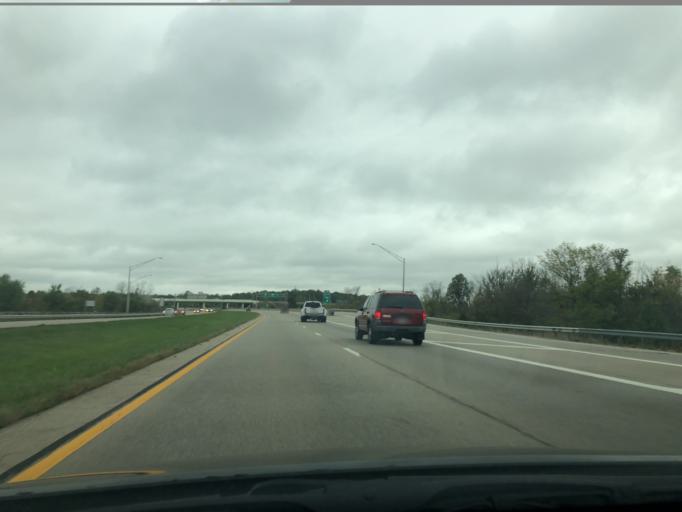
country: US
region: Ohio
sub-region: Union County
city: Marysville
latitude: 40.2508
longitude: -83.3624
